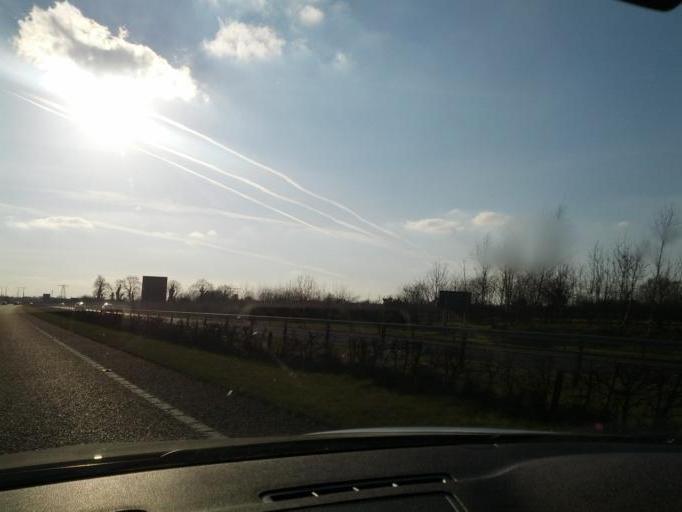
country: IE
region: Leinster
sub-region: Laois
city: Stradbally
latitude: 53.0837
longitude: -7.1841
